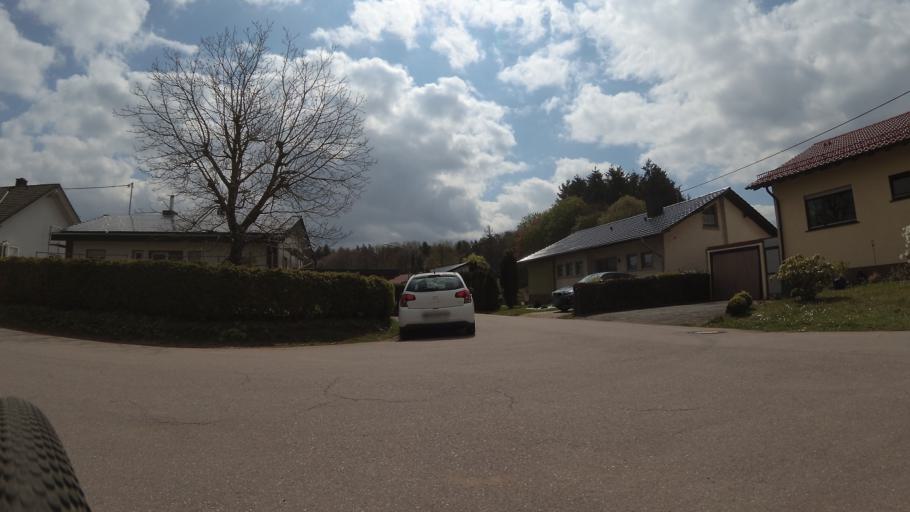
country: DE
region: Saarland
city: Britten
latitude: 49.5211
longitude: 6.6683
